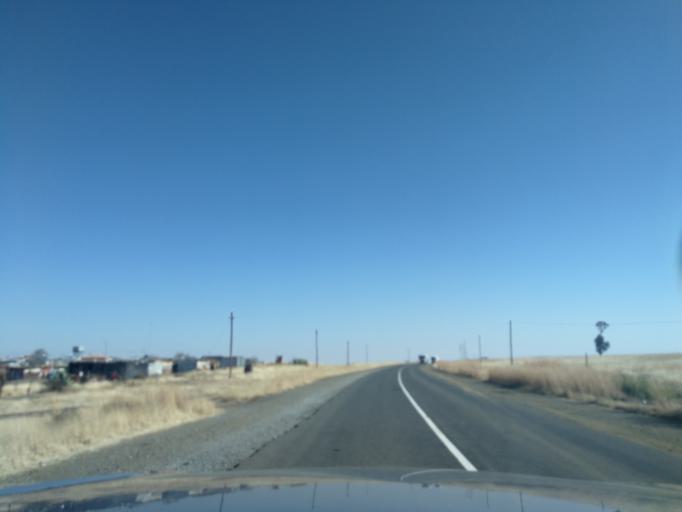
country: ZA
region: Orange Free State
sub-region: Thabo Mofutsanyana District Municipality
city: Senekal
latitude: -27.9402
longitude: 27.5578
